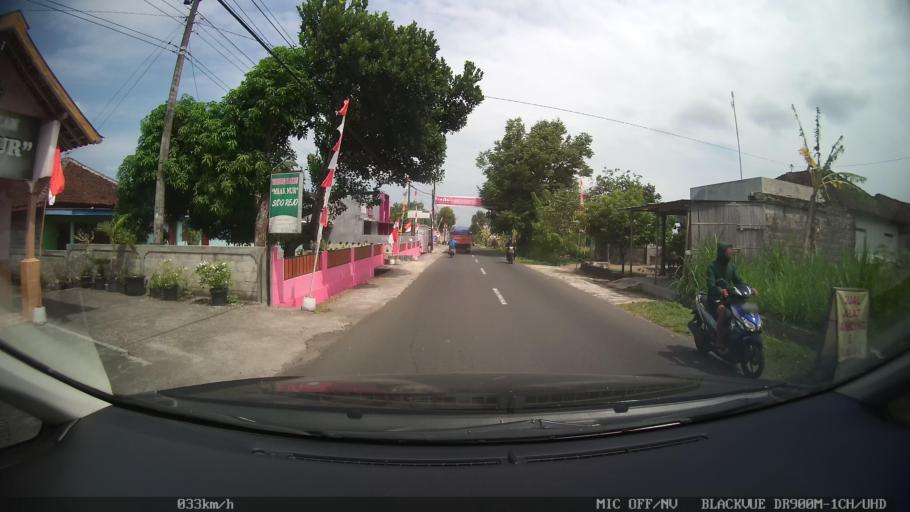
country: ID
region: Daerah Istimewa Yogyakarta
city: Depok
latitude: -7.7311
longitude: 110.4513
